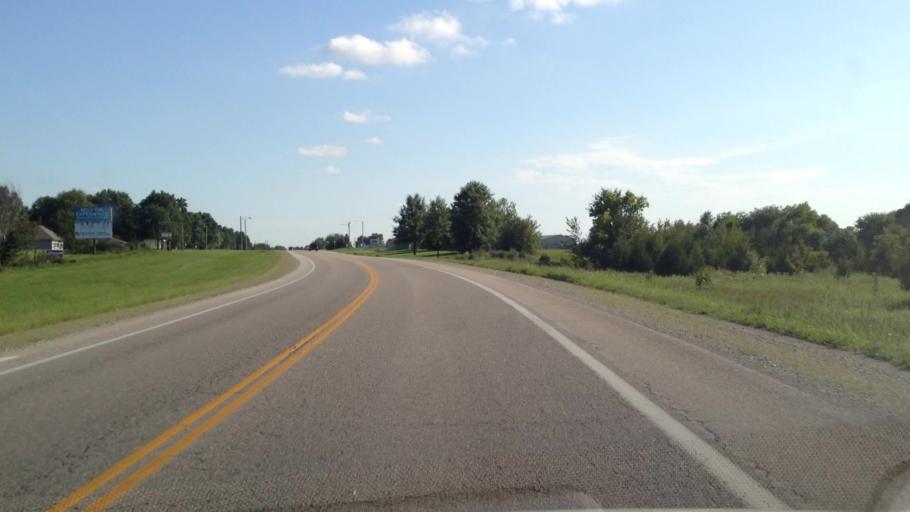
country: US
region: Kansas
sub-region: Crawford County
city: Arma
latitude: 37.5495
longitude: -94.7102
